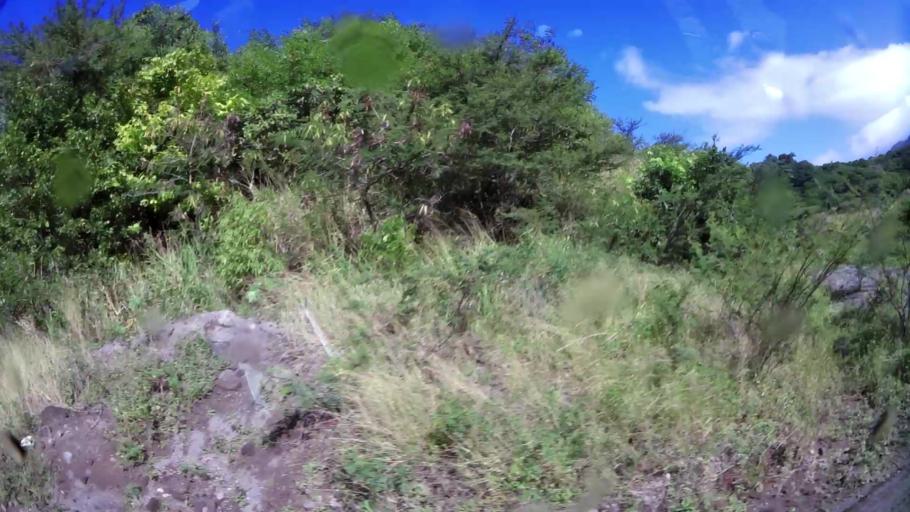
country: MS
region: Saint Peter
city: Saint Peters
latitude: 16.7411
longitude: -62.2209
